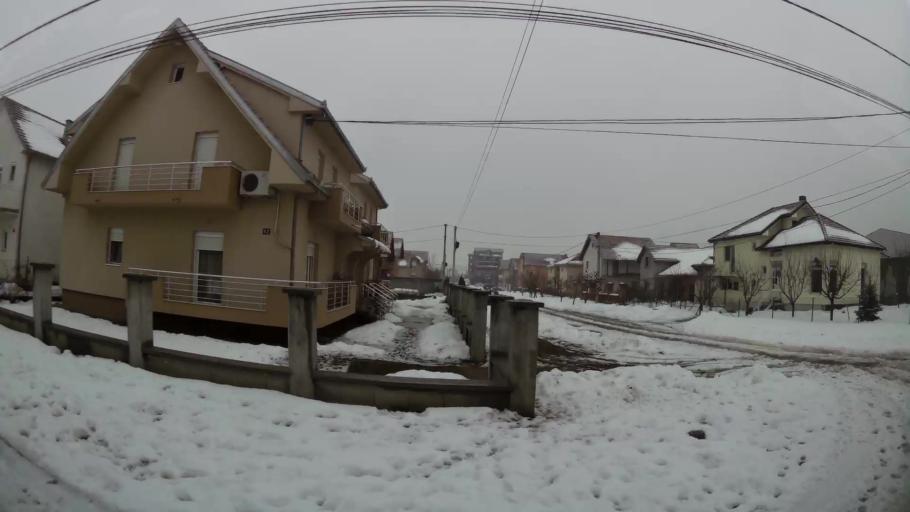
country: RS
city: Novi Banovci
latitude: 44.8768
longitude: 20.3137
